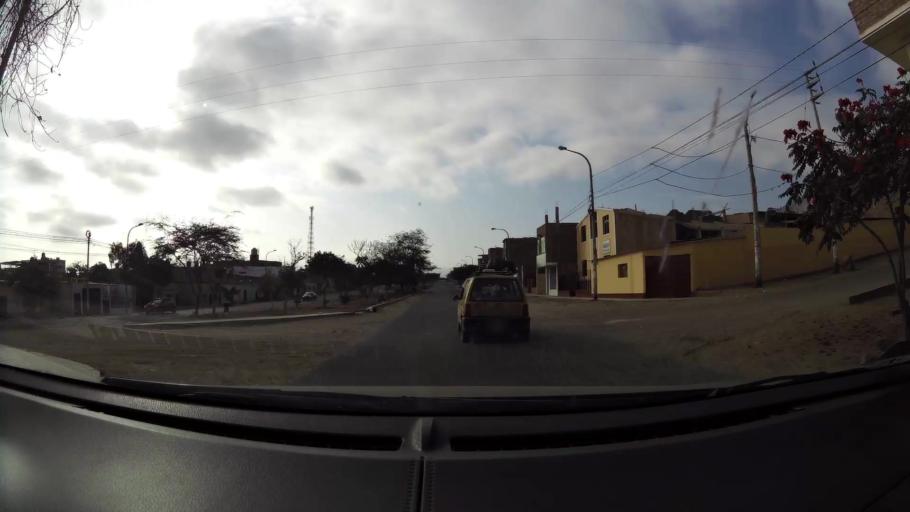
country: PE
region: La Libertad
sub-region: Provincia de Trujillo
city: La Esperanza
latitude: -8.0749
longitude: -79.0459
